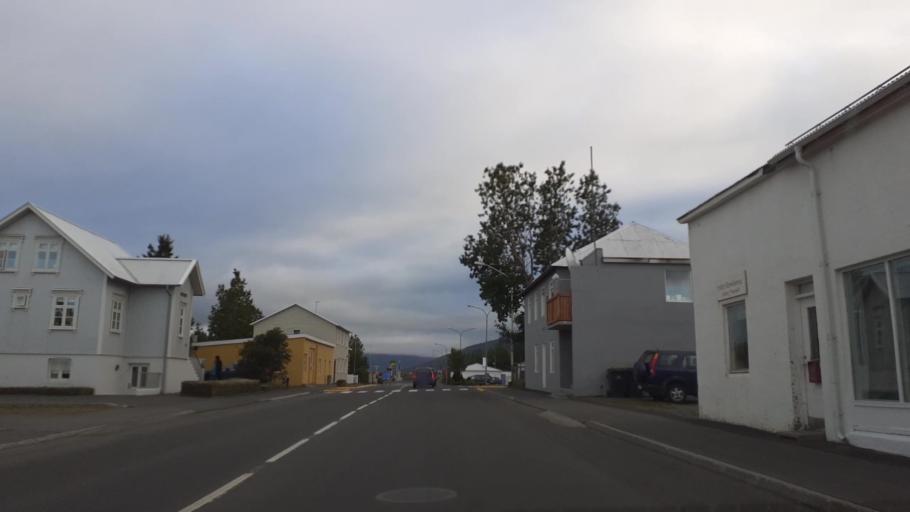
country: IS
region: Northeast
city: Dalvik
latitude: 65.9692
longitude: -18.5276
